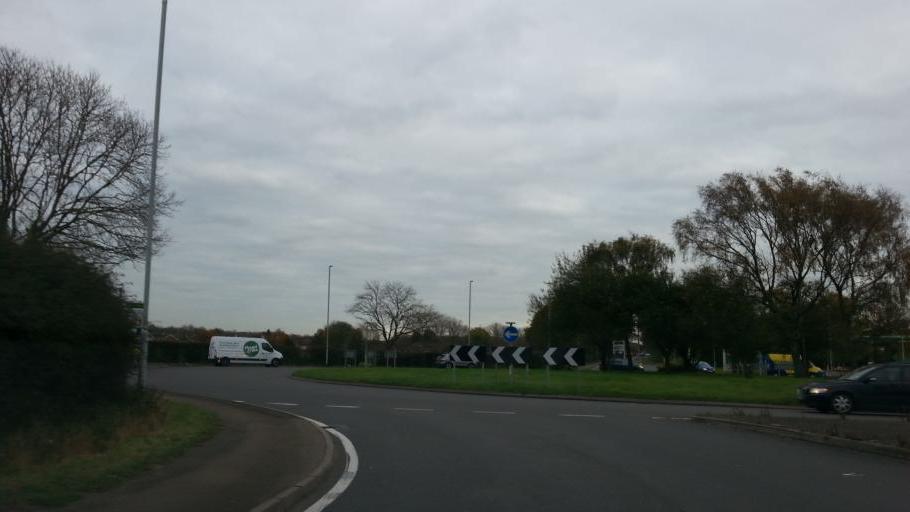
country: GB
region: England
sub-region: Northamptonshire
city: Corby
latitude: 52.4944
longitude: -0.7313
